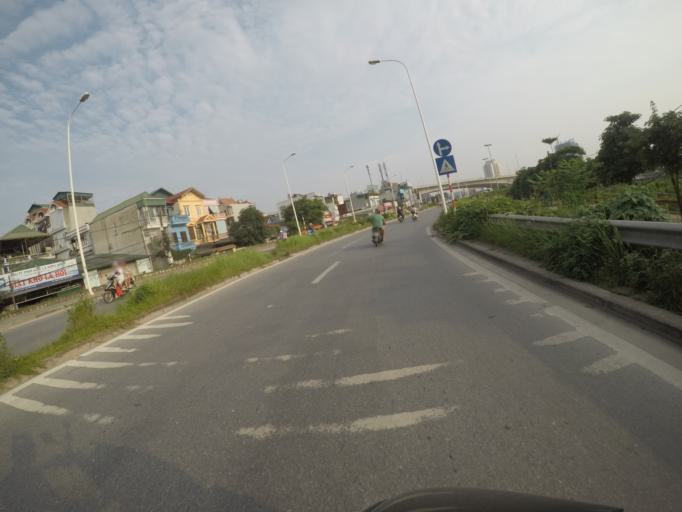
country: VN
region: Ha Noi
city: Tay Ho
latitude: 21.0865
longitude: 105.8160
